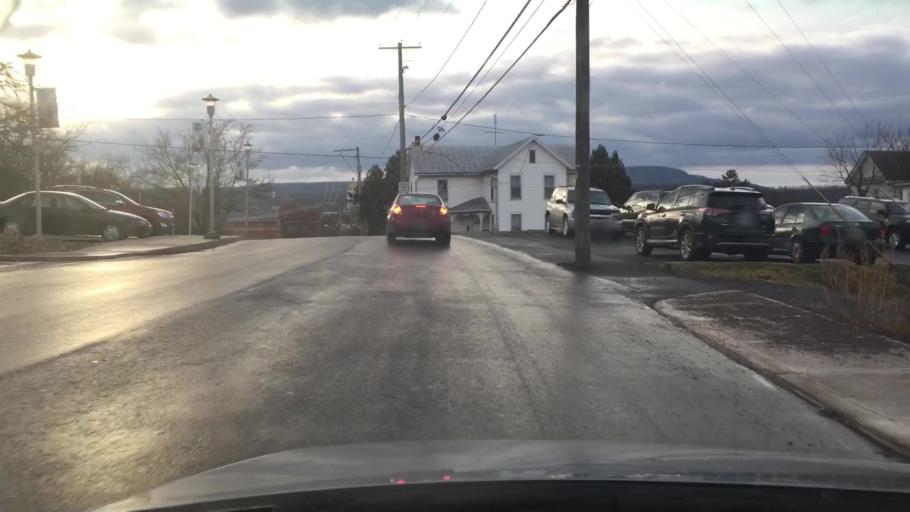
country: US
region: Pennsylvania
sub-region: Columbia County
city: Bloomsburg
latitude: 41.0088
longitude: -76.4536
